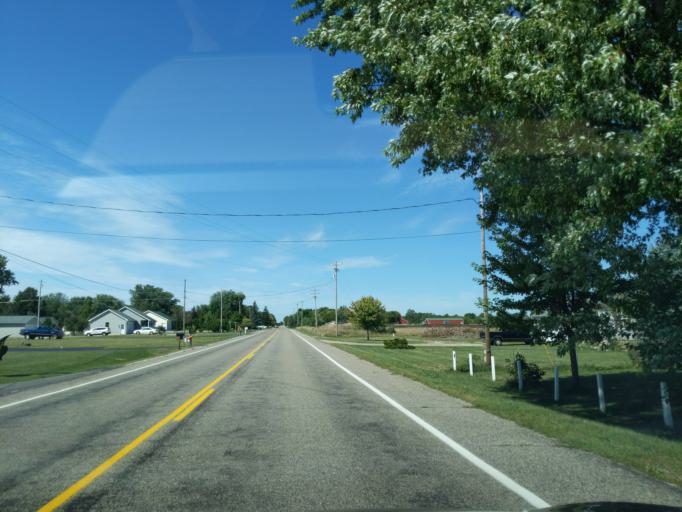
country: US
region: Michigan
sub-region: Eaton County
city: Potterville
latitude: 42.6260
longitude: -84.7881
